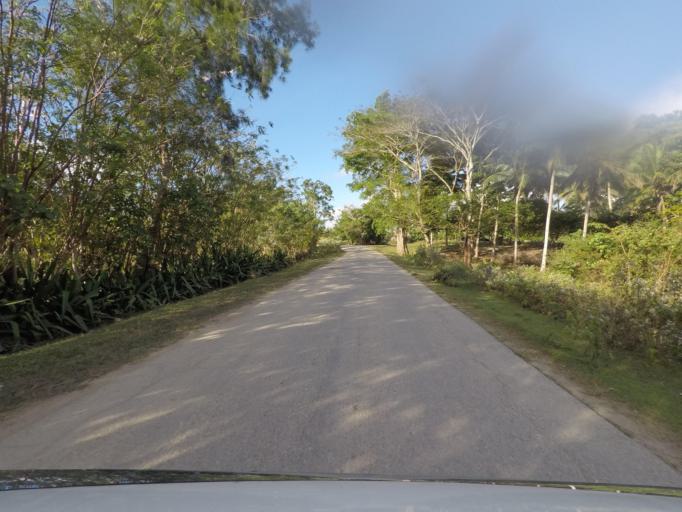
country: TL
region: Lautem
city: Lospalos
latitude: -8.4573
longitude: 127.0005
